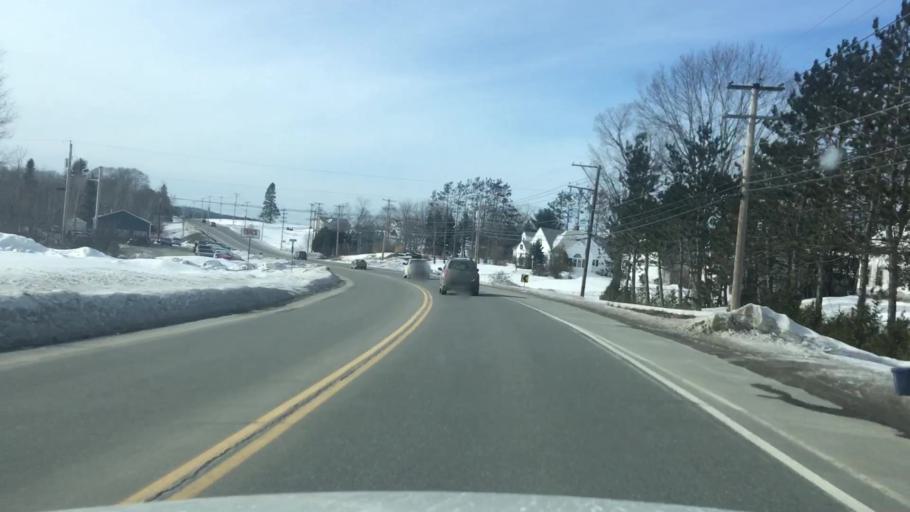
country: US
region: Maine
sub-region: Penobscot County
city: Bangor
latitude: 44.8516
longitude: -68.8063
